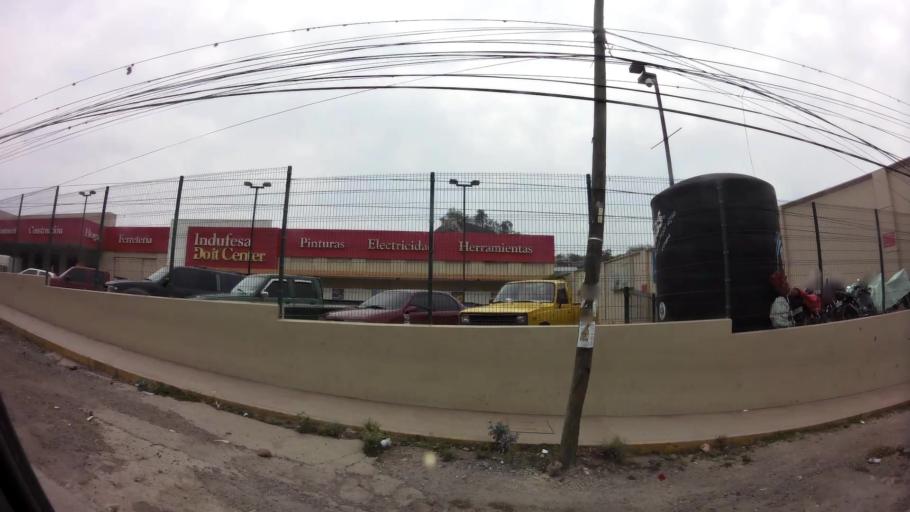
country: HN
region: Francisco Morazan
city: Tegucigalpa
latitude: 14.0660
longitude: -87.2103
